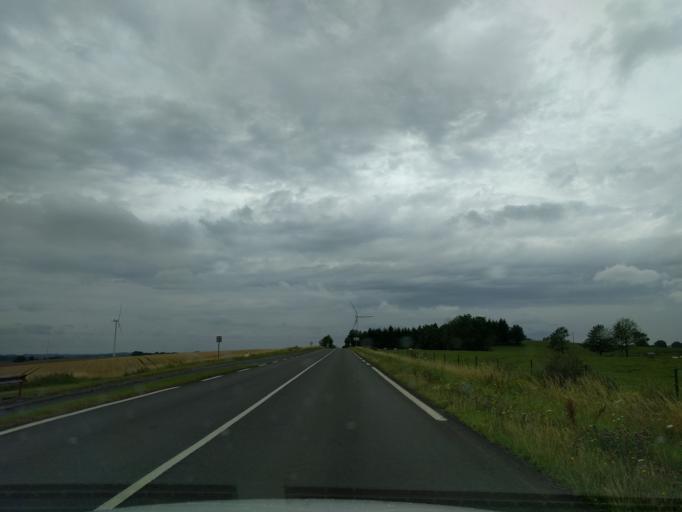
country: FR
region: Champagne-Ardenne
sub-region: Departement des Ardennes
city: Signy-le-Petit
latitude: 49.8678
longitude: 4.3036
